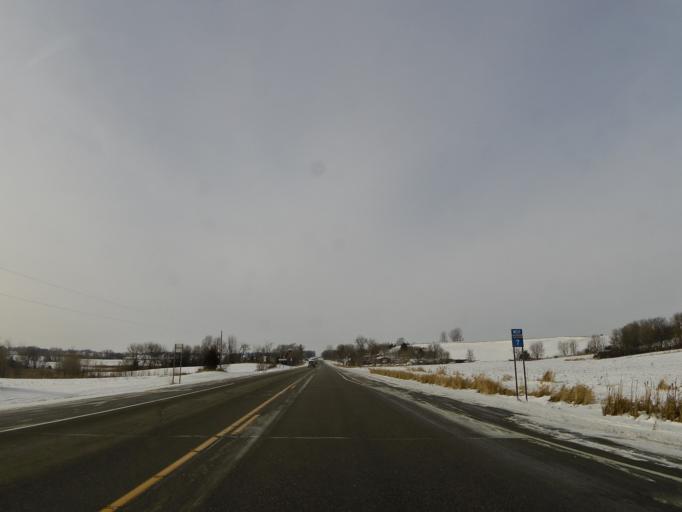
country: US
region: Minnesota
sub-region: Hennepin County
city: Saint Bonifacius
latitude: 44.9053
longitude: -93.7850
